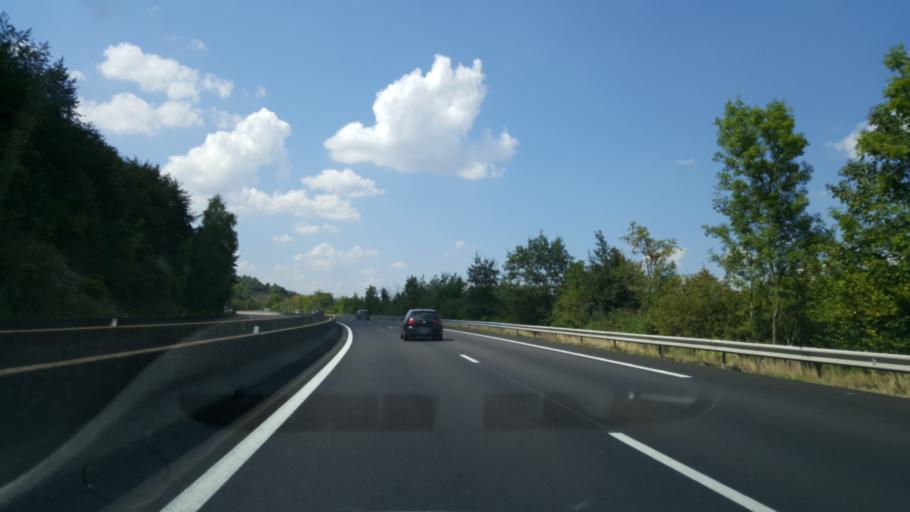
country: FR
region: Bourgogne
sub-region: Departement de la Cote-d'Or
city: Pouilly-en-Auxois
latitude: 47.1745
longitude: 4.6893
